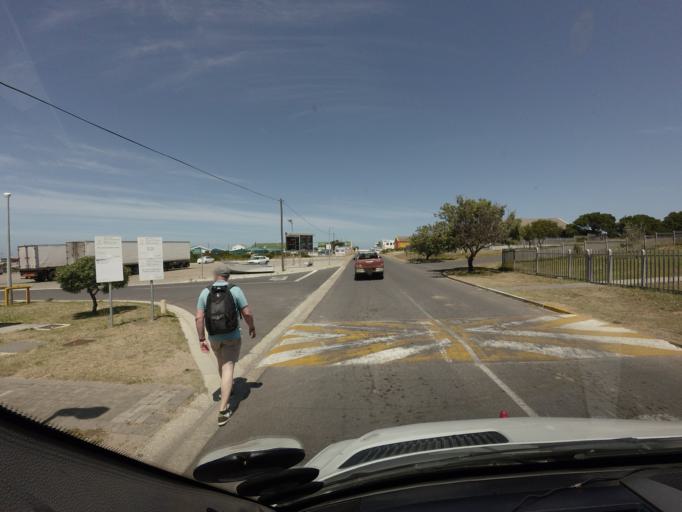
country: ZA
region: Western Cape
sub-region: Overberg District Municipality
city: Hermanus
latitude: -34.4333
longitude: 19.2236
